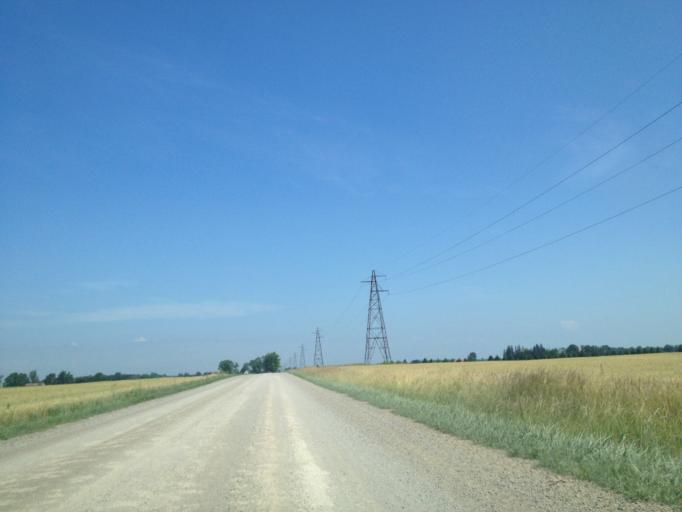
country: CA
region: Ontario
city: London
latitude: 43.1140
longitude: -81.2314
